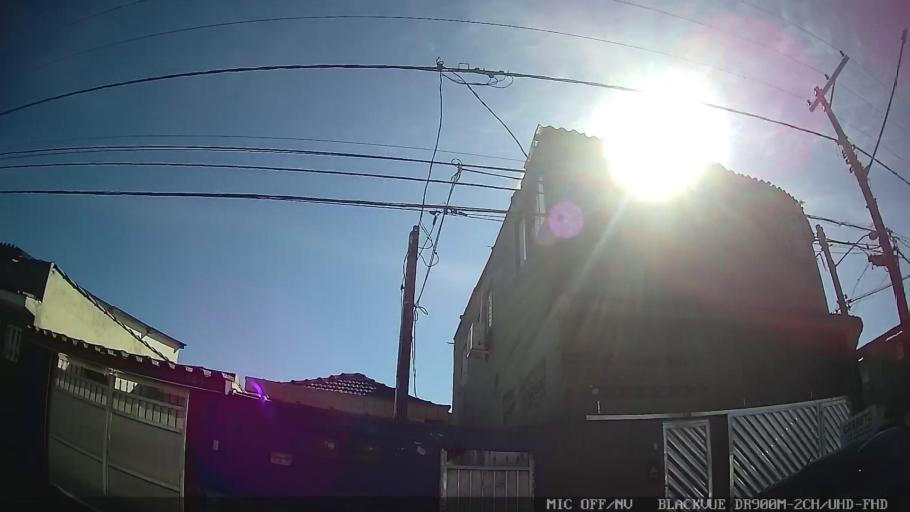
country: BR
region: Sao Paulo
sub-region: Santos
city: Santos
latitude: -23.9450
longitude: -46.2872
